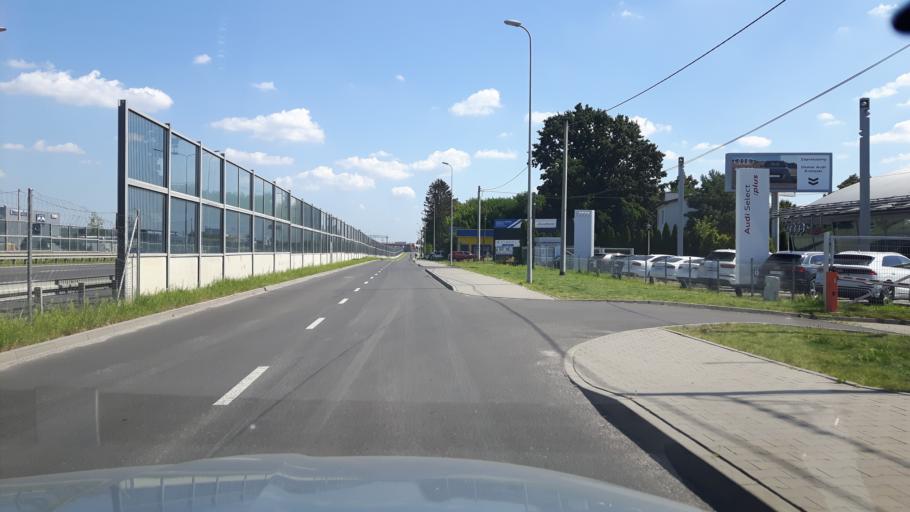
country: PL
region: Masovian Voivodeship
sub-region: Powiat pruszkowski
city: Komorow
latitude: 52.1146
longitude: 20.8586
